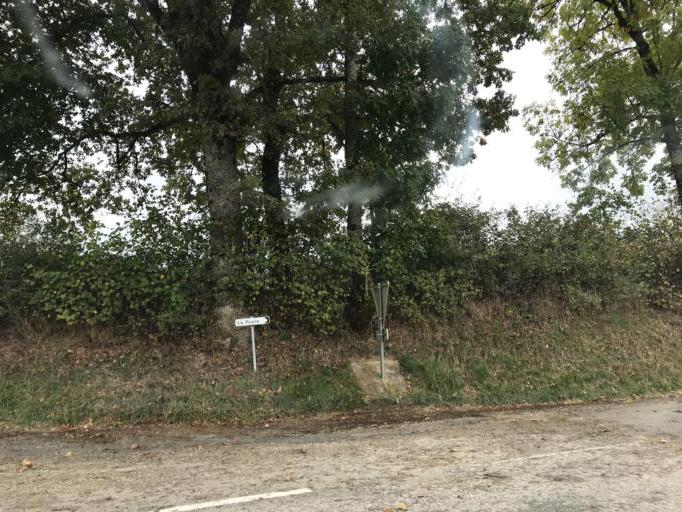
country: FR
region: Rhone-Alpes
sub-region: Departement de l'Ain
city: Cuisiat
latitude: 46.3393
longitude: 5.4393
